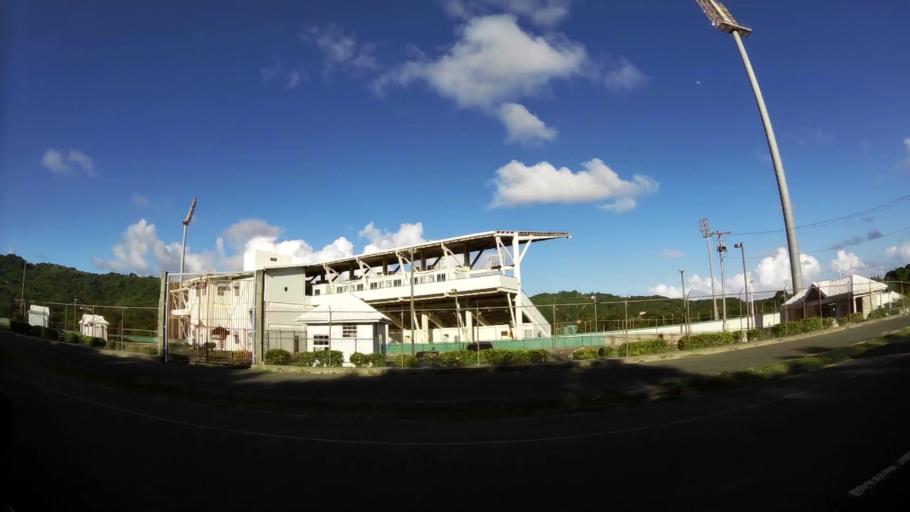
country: TT
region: Tobago
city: Scarborough
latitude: 11.1808
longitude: -60.7179
